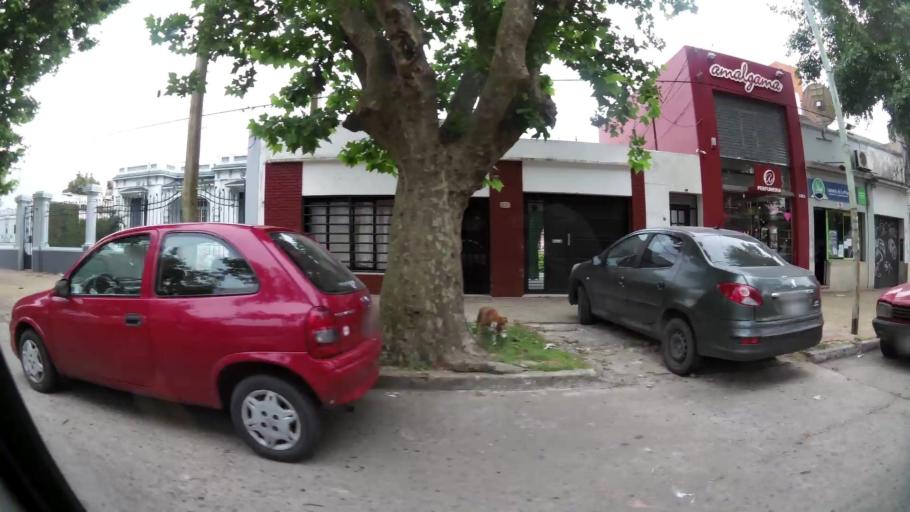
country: AR
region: Buenos Aires
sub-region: Partido de La Plata
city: La Plata
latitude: -34.9344
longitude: -57.9565
